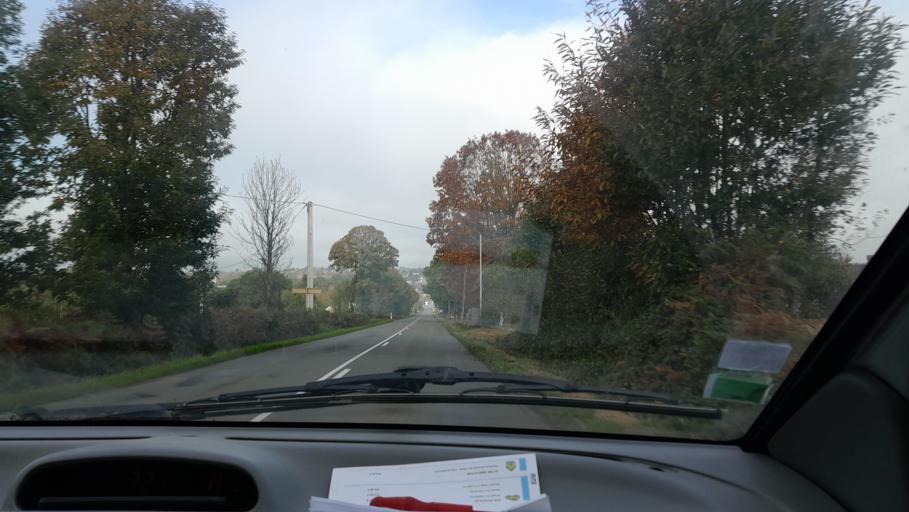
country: FR
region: Brittany
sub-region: Departement d'Ille-et-Vilaine
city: Luitre
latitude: 48.2608
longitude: -1.1327
